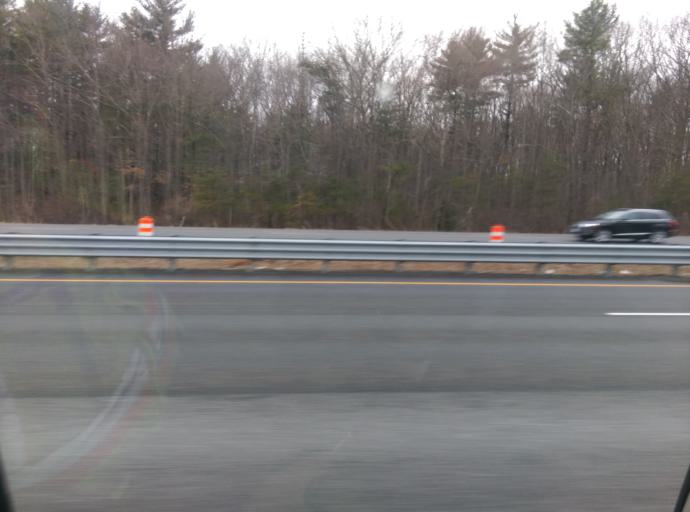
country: US
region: Massachusetts
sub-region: Essex County
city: Amesbury
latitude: 42.8531
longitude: -70.8982
